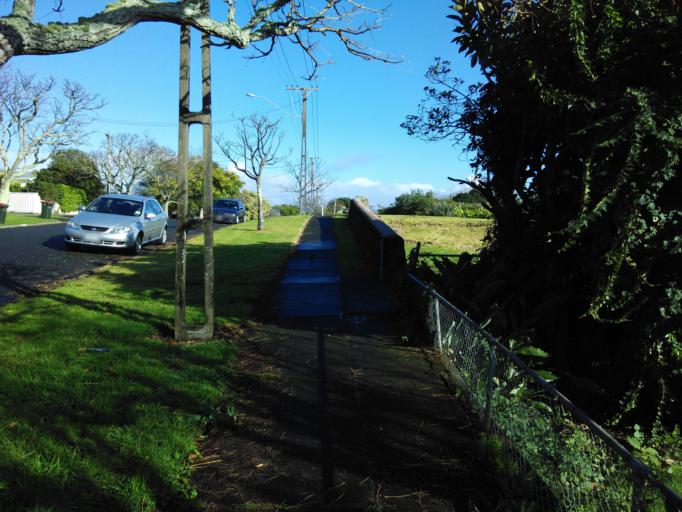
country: NZ
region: Auckland
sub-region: Auckland
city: Mangere
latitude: -36.9204
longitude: 174.7978
